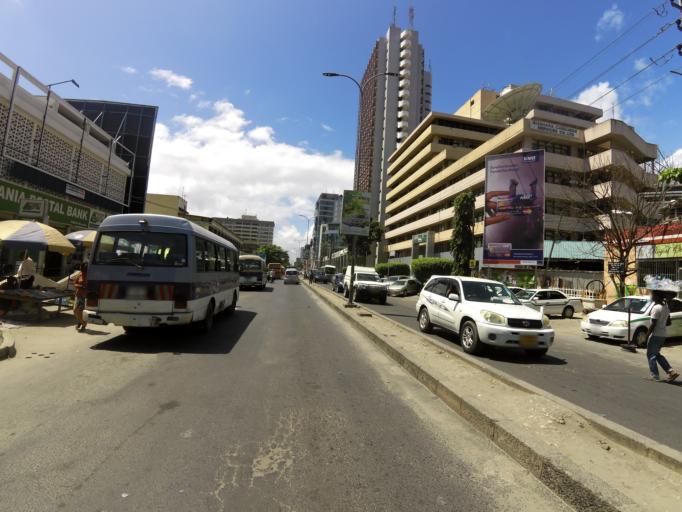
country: TZ
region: Dar es Salaam
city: Dar es Salaam
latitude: -6.8142
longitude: 39.2874
